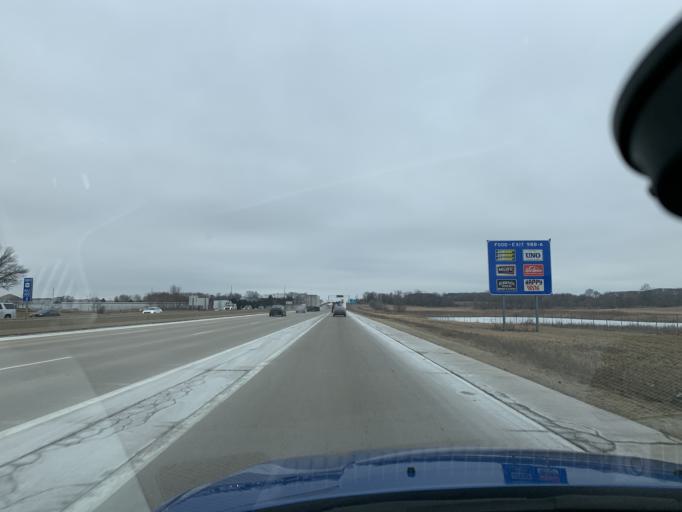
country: US
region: Wisconsin
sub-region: Dane County
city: Sun Prairie
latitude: 43.1594
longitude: -89.2702
